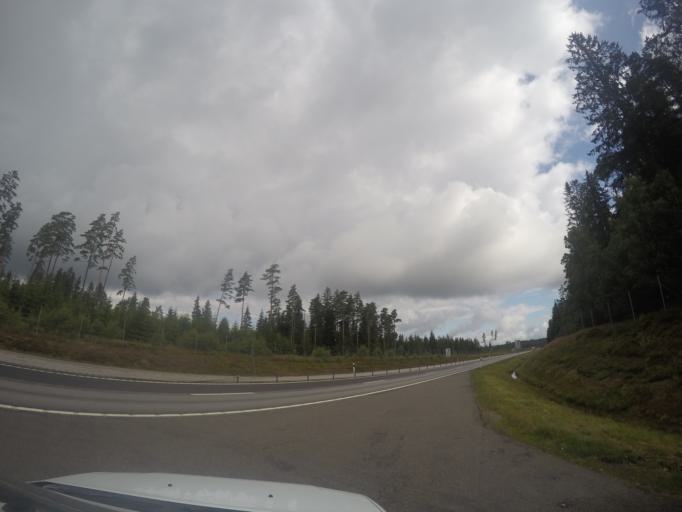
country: SE
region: Kronoberg
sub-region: Ljungby Kommun
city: Ljungby
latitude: 56.7847
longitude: 13.8843
